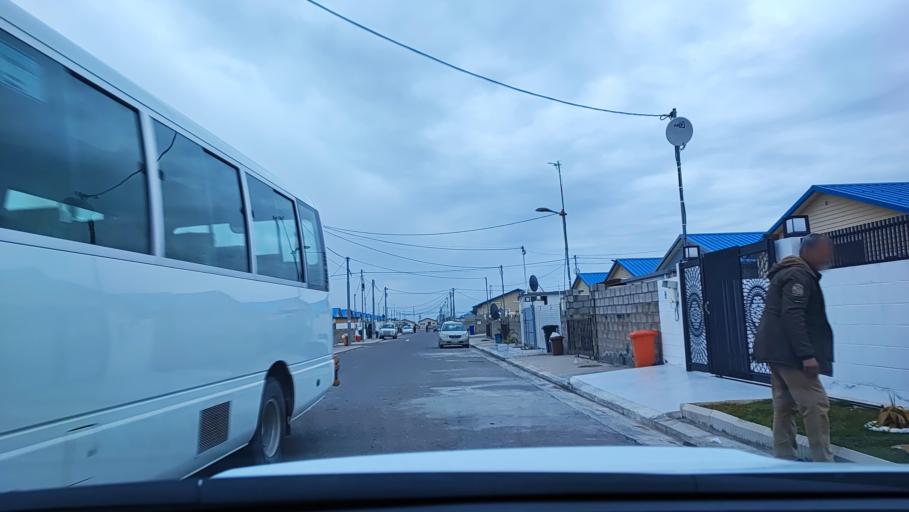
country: IQ
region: Arbil
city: Erbil
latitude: 36.2850
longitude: 44.0809
